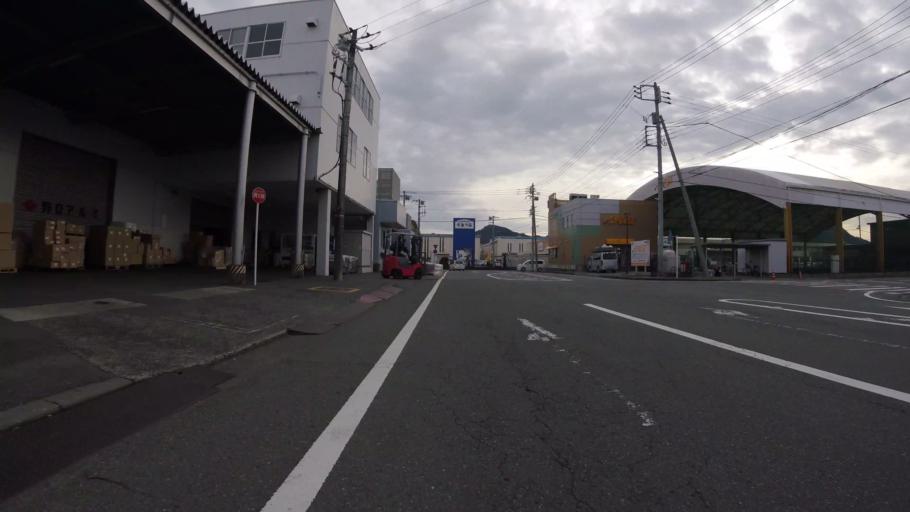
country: JP
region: Shizuoka
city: Mishima
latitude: 35.0938
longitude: 138.9093
